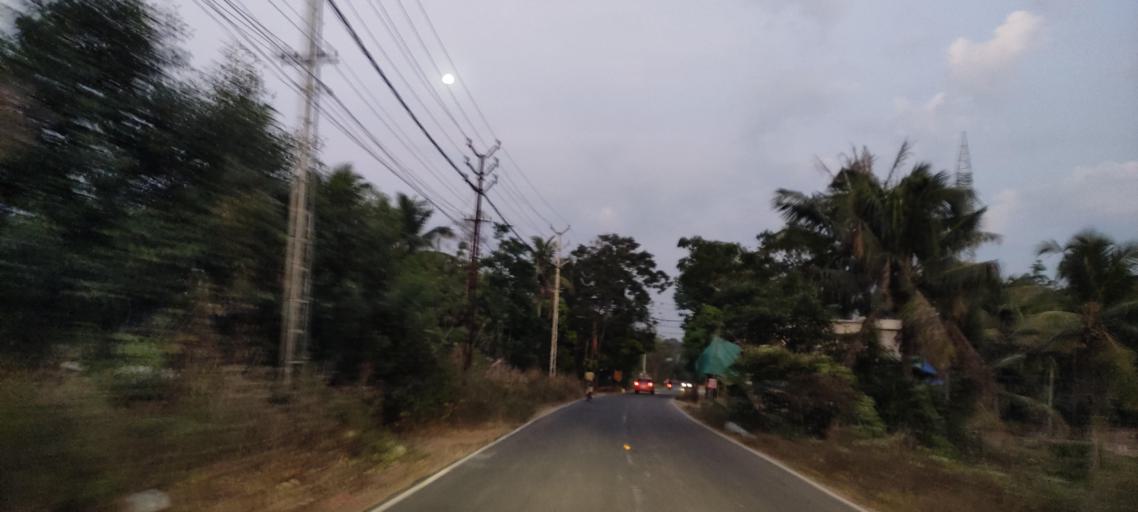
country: IN
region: Kerala
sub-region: Alappuzha
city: Kutiatodu
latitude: 9.7737
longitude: 76.3559
